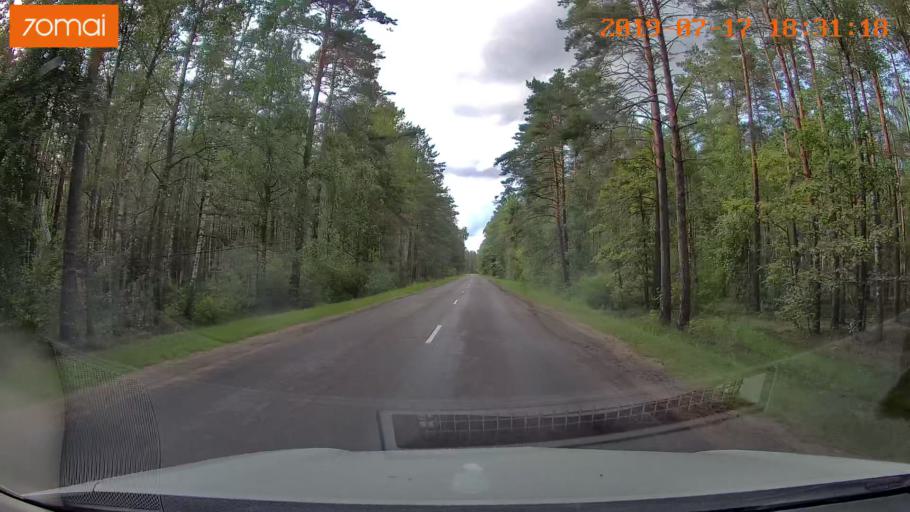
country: BY
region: Mogilev
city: Asipovichy
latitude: 53.2575
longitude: 28.6835
